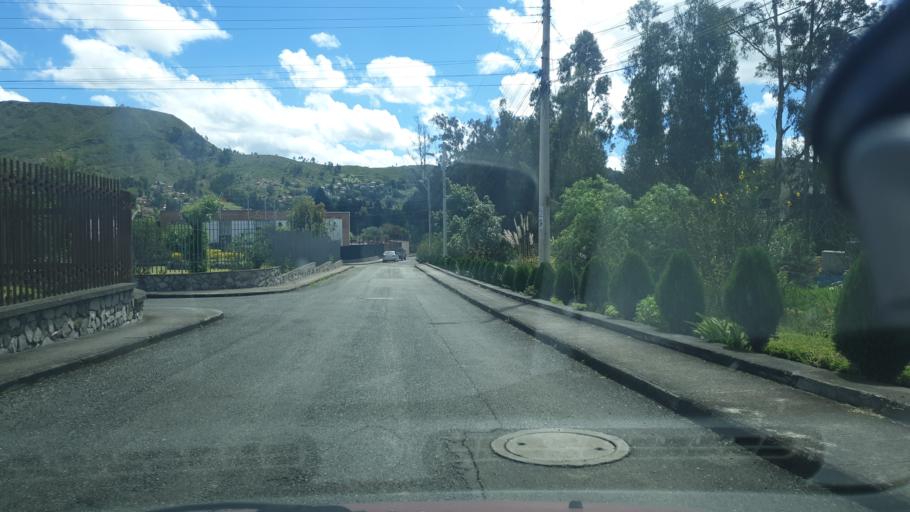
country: EC
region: Azuay
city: Llacao
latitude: -2.8549
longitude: -78.9083
